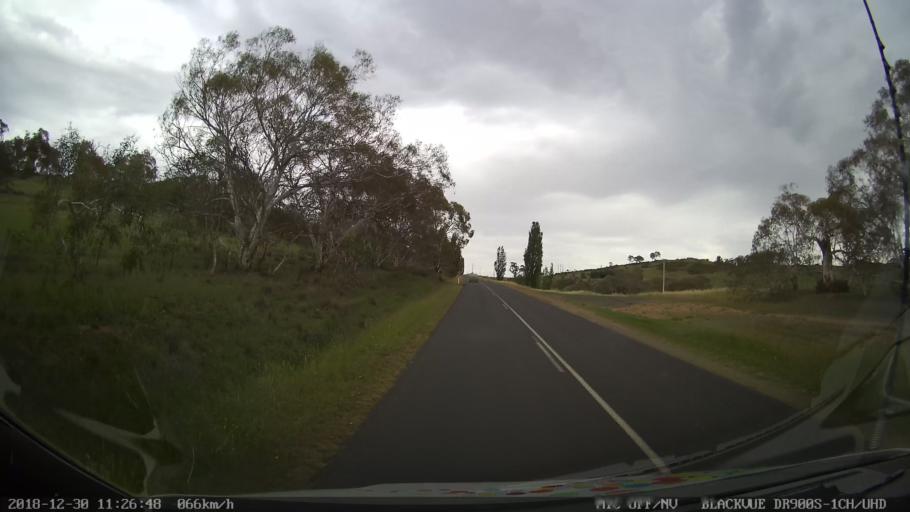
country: AU
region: New South Wales
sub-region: Snowy River
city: Jindabyne
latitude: -36.4655
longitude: 148.6309
